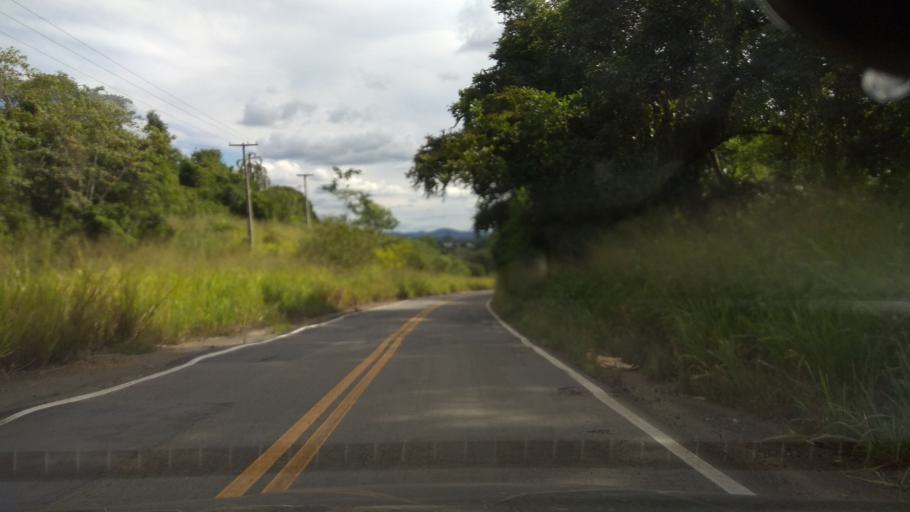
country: BR
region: Bahia
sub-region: Ubata
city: Ubata
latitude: -14.2304
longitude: -39.4523
